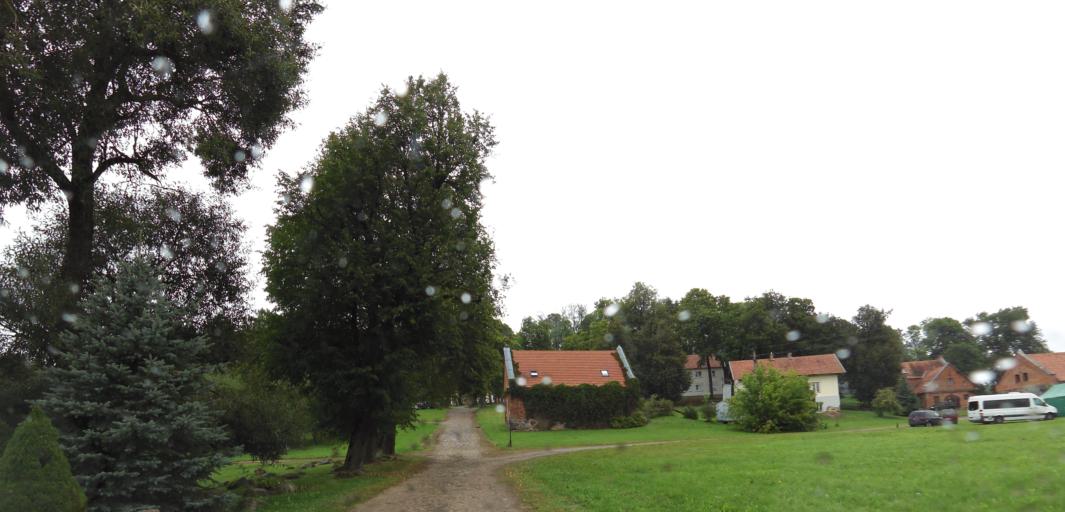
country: LT
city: Sirvintos
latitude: 55.0759
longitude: 25.0614
